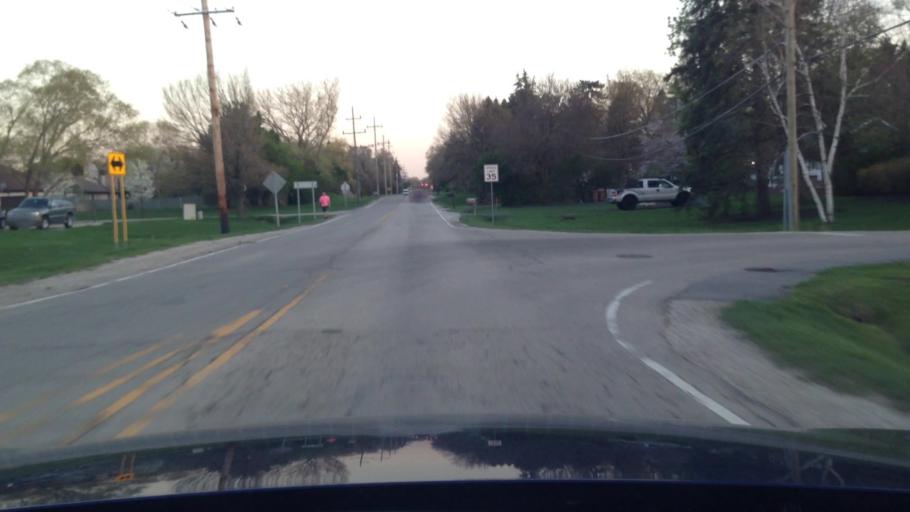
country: US
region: Illinois
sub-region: Cook County
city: Prospect Heights
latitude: 42.1027
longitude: -87.9272
